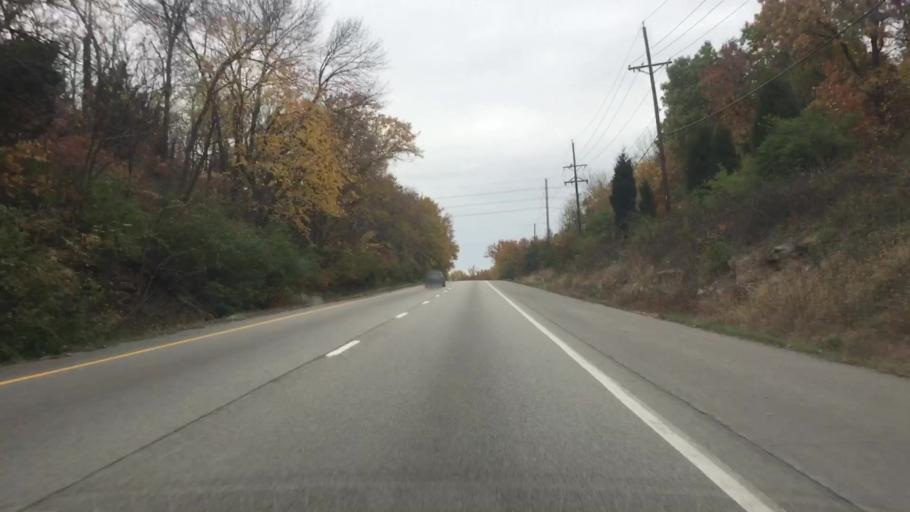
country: US
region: Missouri
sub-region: Jackson County
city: Raytown
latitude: 38.9700
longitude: -94.4372
